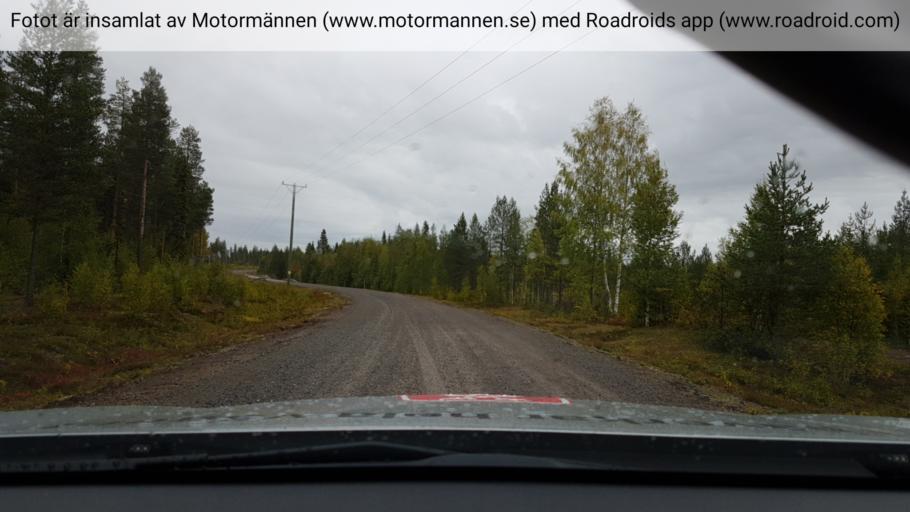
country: SE
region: Vaesterbotten
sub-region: Norsjo Kommun
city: Norsjoe
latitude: 65.2837
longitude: 19.8728
